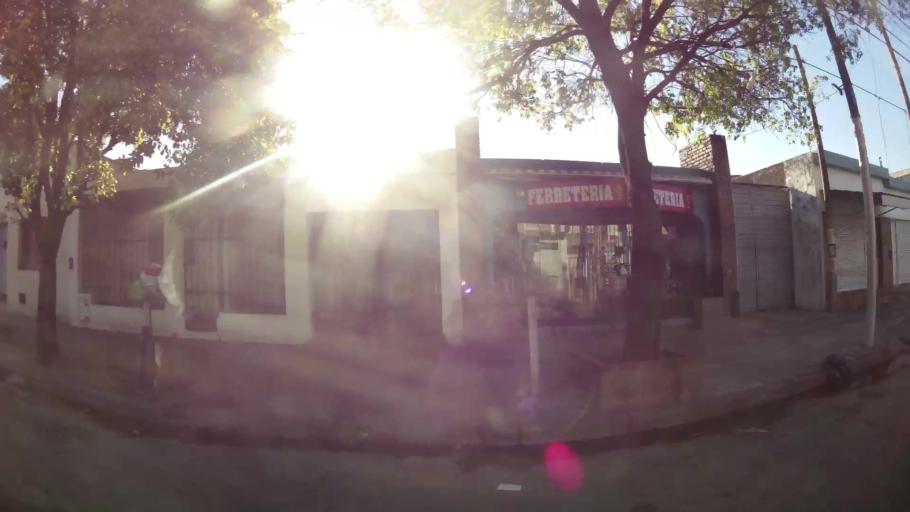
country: AR
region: Cordoba
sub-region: Departamento de Capital
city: Cordoba
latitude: -31.3791
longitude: -64.1839
